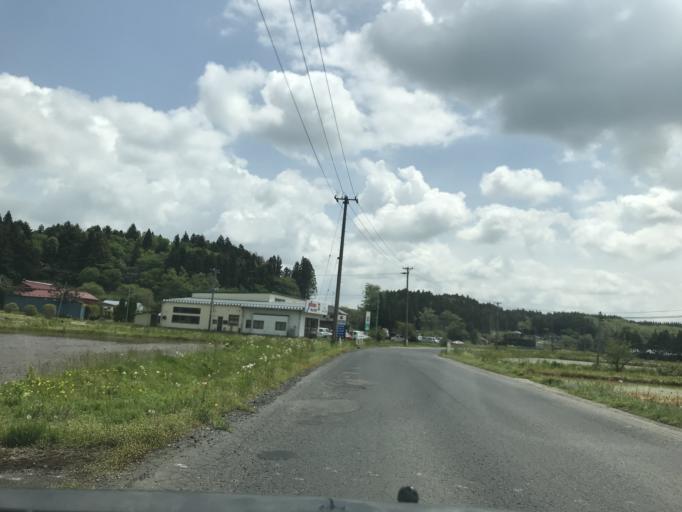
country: JP
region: Miyagi
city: Furukawa
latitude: 38.7035
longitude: 140.9205
